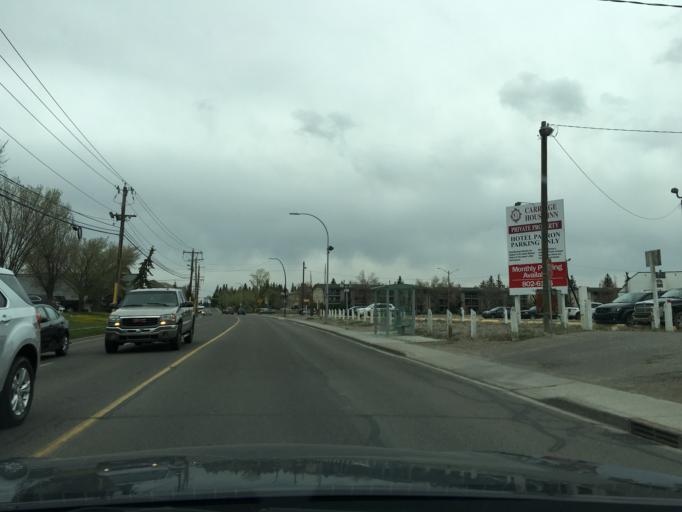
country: CA
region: Alberta
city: Calgary
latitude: 50.9724
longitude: -114.0687
